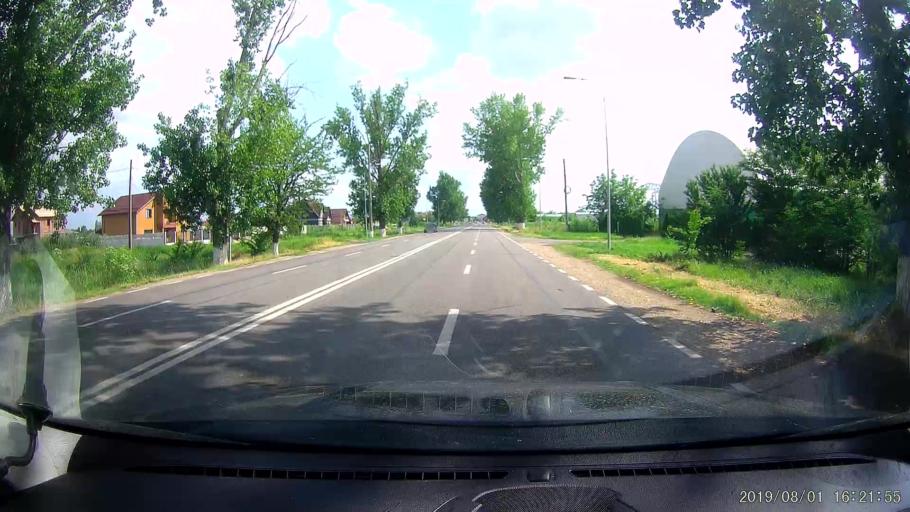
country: RO
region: Calarasi
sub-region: Municipiul Calarasi
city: Calarasi
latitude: 44.2102
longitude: 27.3386
